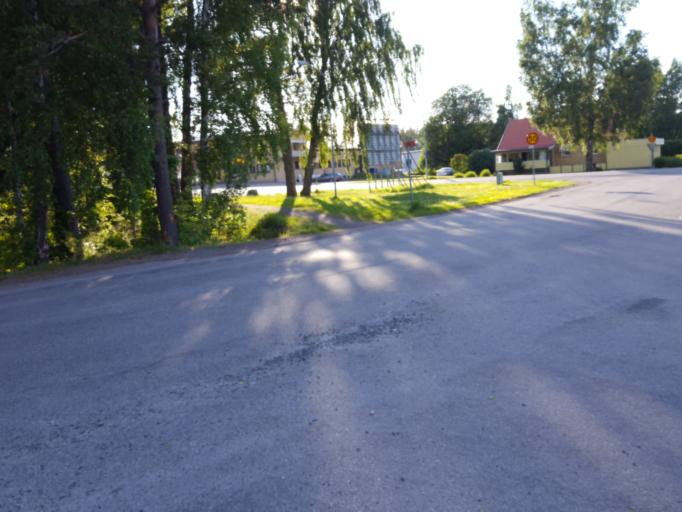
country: SE
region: Uppsala
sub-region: Osthammars Kommun
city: OEsthammar
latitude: 60.2559
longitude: 18.3497
